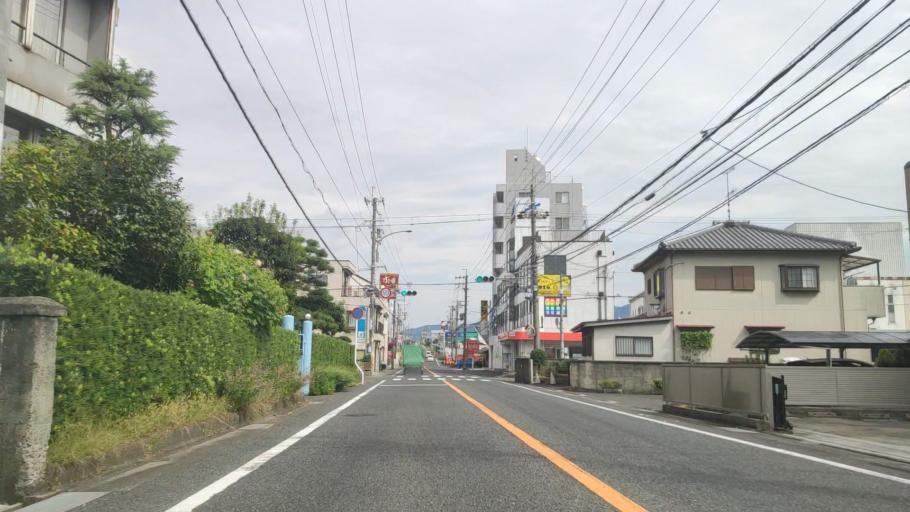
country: JP
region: Wakayama
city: Hashimoto
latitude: 34.3026
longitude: 135.5573
